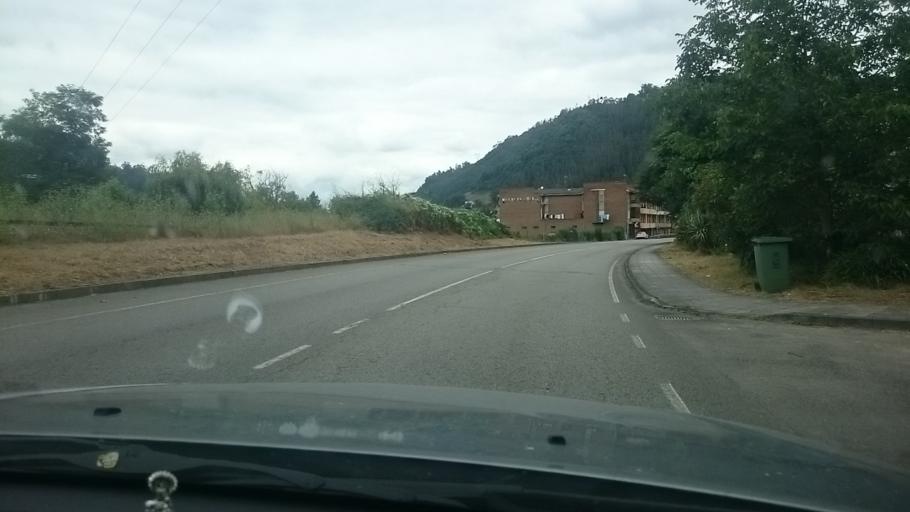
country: ES
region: Asturias
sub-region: Province of Asturias
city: Mieres
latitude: 43.2067
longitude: -5.7870
